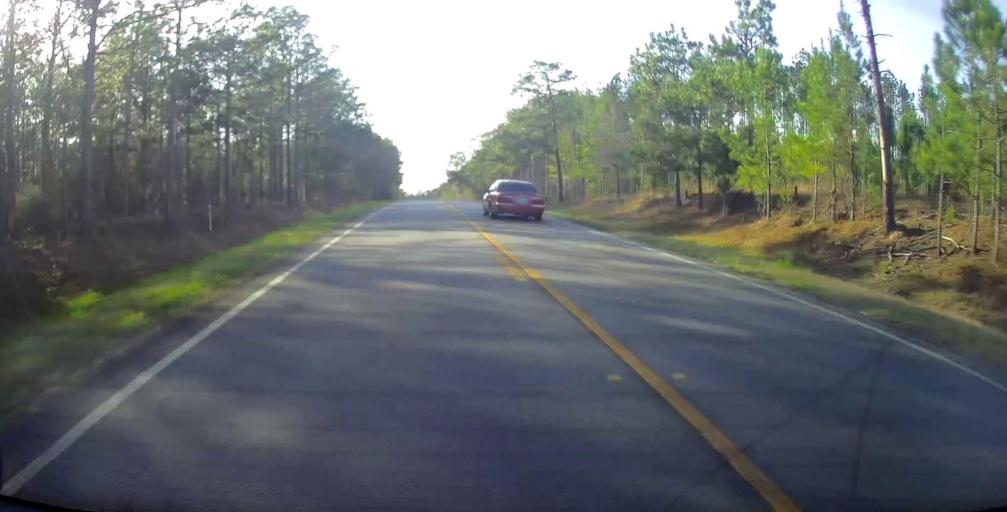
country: US
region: Georgia
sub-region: Toombs County
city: Lyons
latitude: 32.1414
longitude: -82.2465
